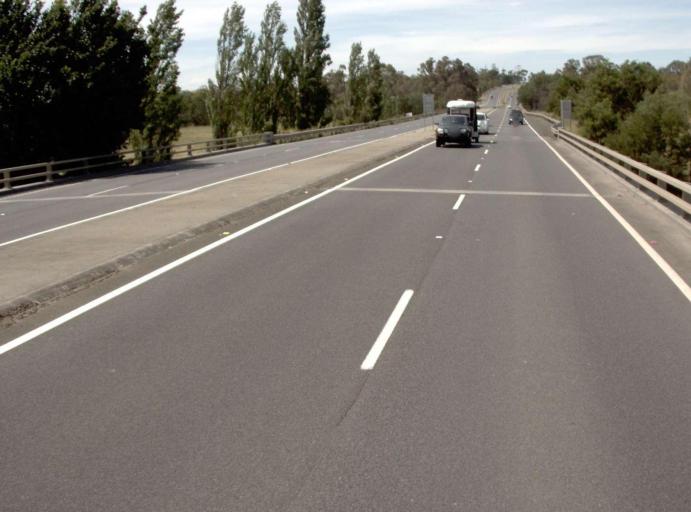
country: AU
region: Victoria
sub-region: Wellington
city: Heyfield
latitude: -38.1457
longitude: 146.7914
